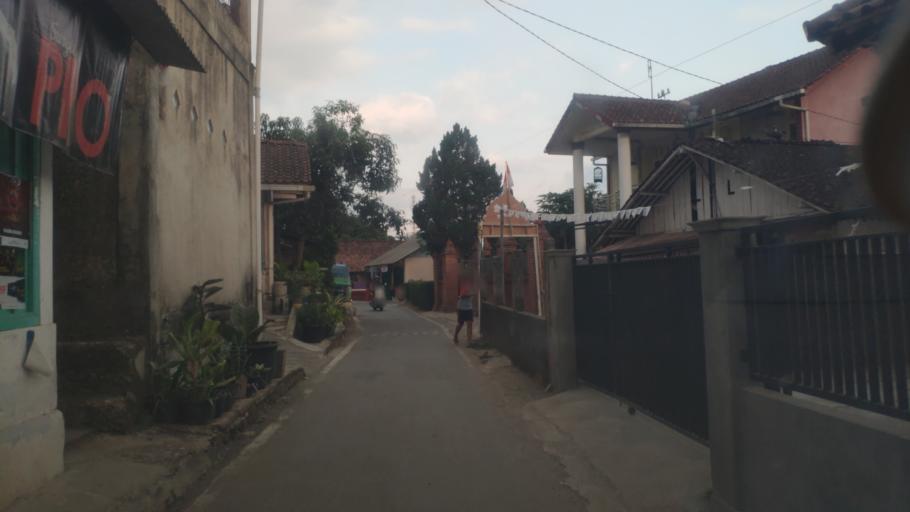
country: ID
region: Central Java
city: Wonosobo
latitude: -7.3931
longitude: 109.7070
